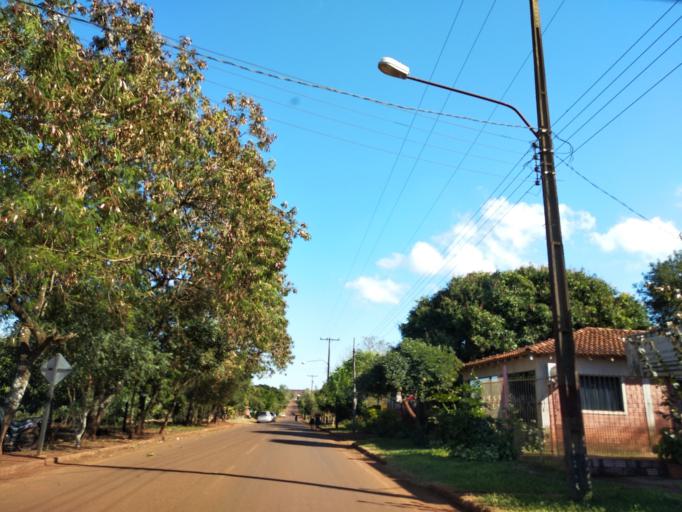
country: PY
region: Itapua
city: Hohenau
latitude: -27.0556
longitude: -55.7457
